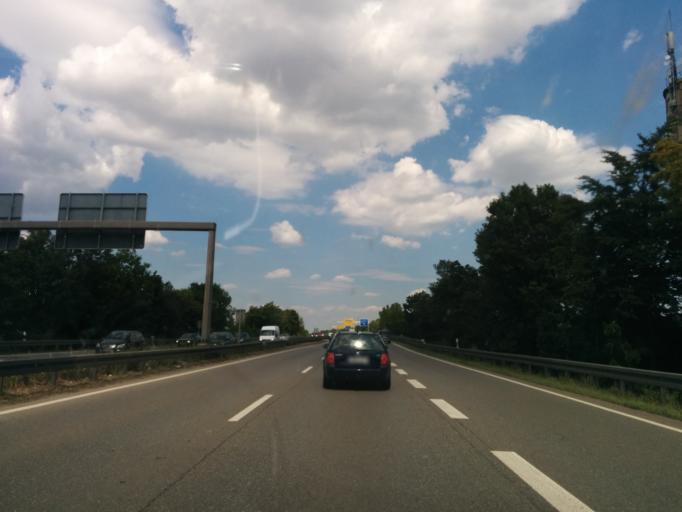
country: DE
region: Bavaria
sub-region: Swabia
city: Gersthofen
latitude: 48.4100
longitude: 10.8738
